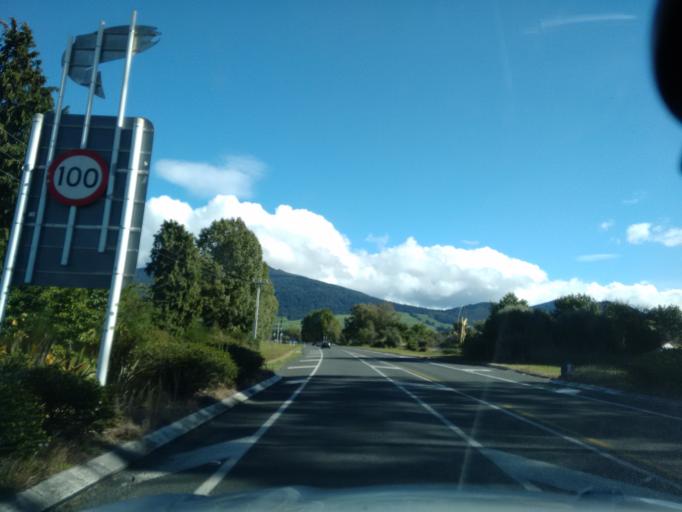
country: NZ
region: Waikato
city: Turangi
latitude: -38.9926
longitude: 175.8079
